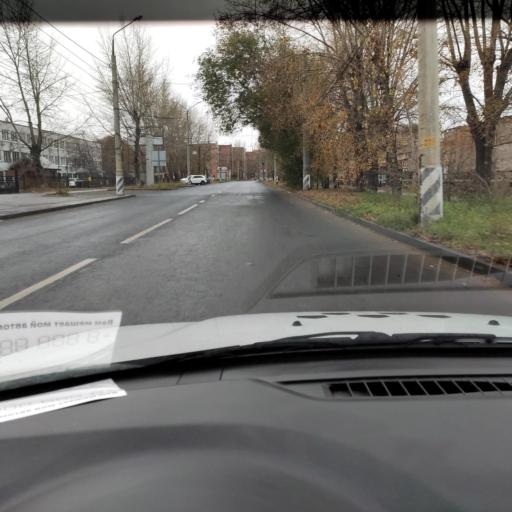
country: RU
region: Samara
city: Tol'yatti
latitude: 53.5162
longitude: 49.4563
